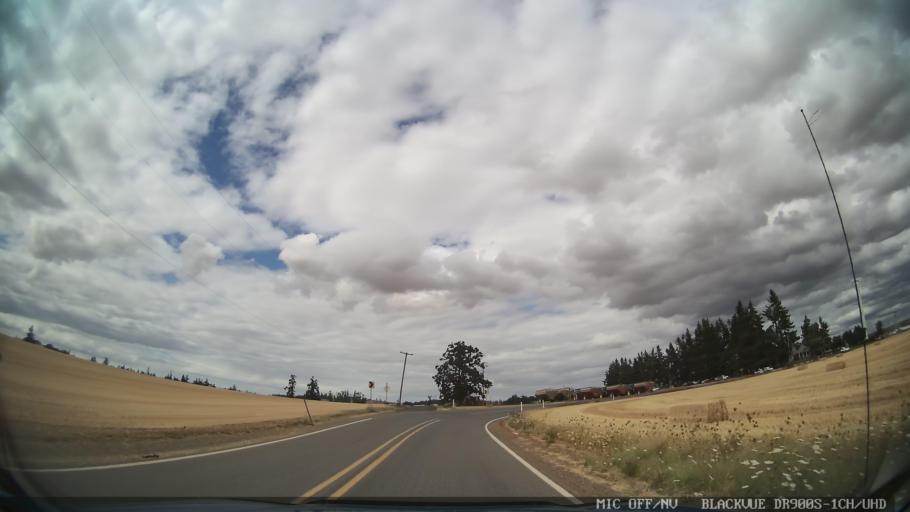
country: US
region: Oregon
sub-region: Marion County
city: Sublimity
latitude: 44.8659
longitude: -122.8107
